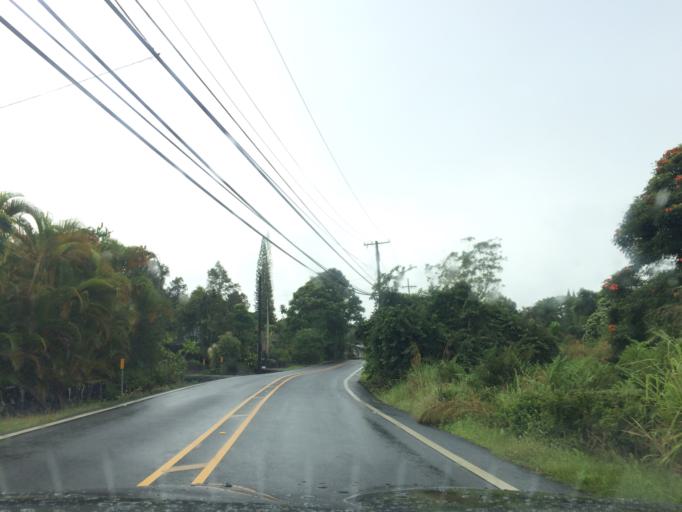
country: US
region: Hawaii
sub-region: Hawaii County
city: Hilo
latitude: 19.6893
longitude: -155.1273
